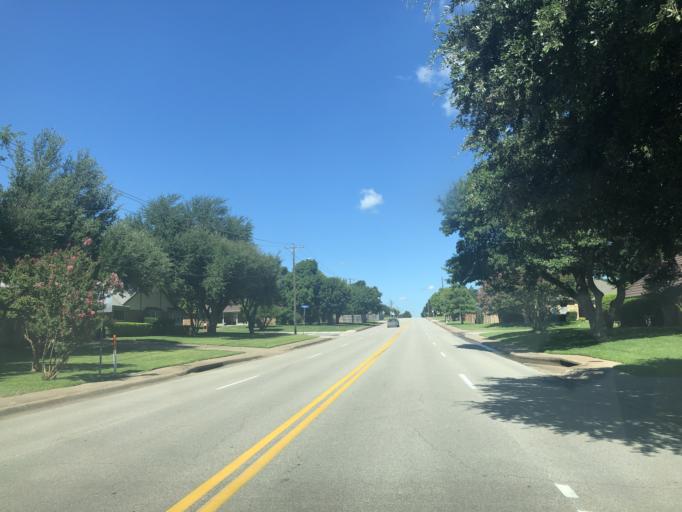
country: US
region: Texas
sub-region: Dallas County
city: Duncanville
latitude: 32.6416
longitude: -96.9279
